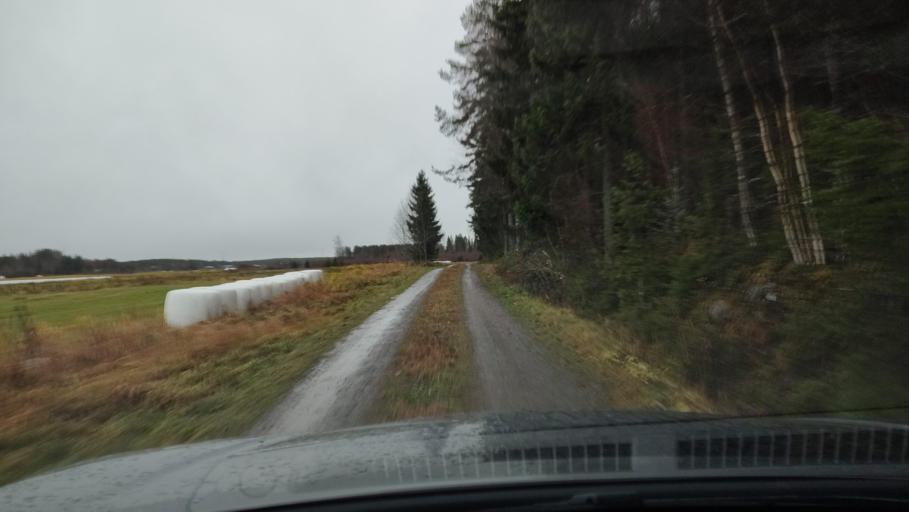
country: FI
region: Southern Ostrobothnia
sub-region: Suupohja
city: Karijoki
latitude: 62.2289
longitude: 21.5517
